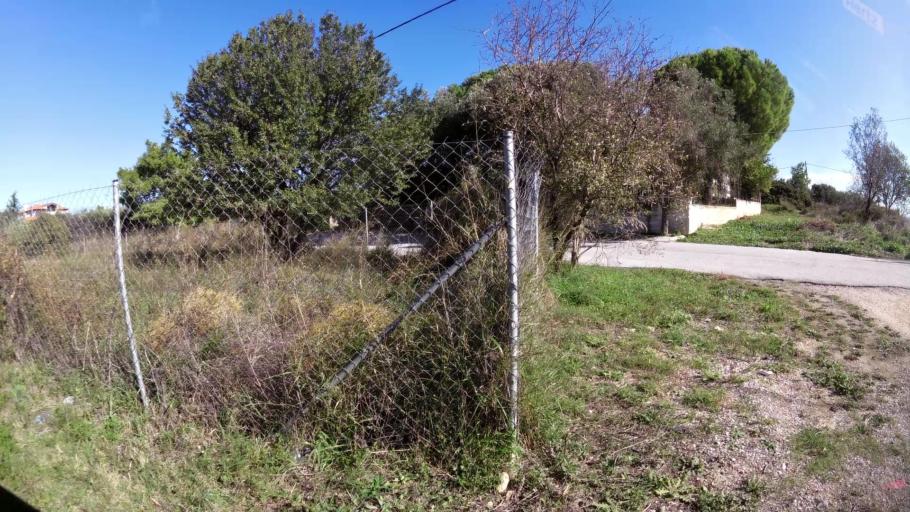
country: GR
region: Attica
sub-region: Nomarchia Anatolikis Attikis
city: Dhrafi
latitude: 38.0066
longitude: 23.9062
